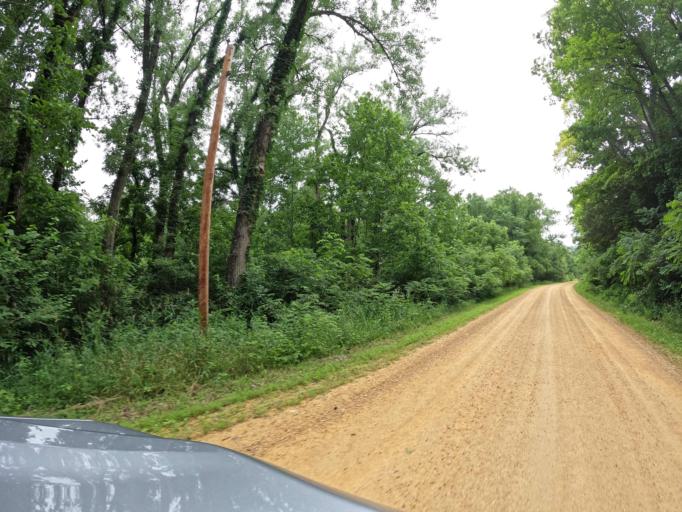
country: US
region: Illinois
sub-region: Carroll County
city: Savanna
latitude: 41.9989
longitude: -90.1748
